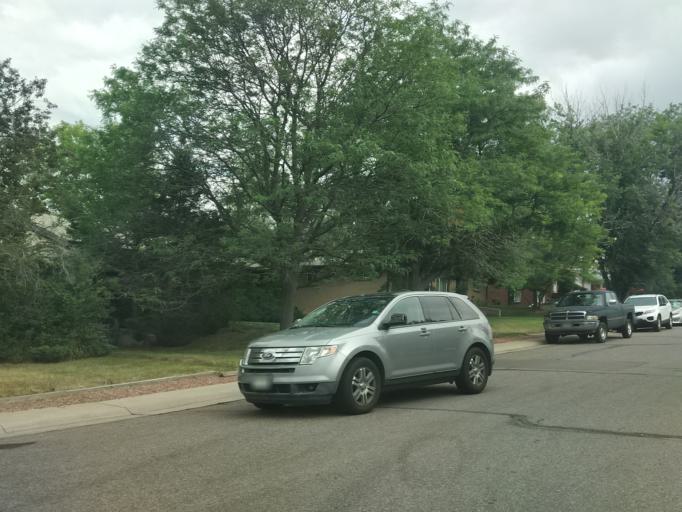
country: US
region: Colorado
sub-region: Jefferson County
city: Lakewood
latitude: 39.7001
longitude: -105.0840
